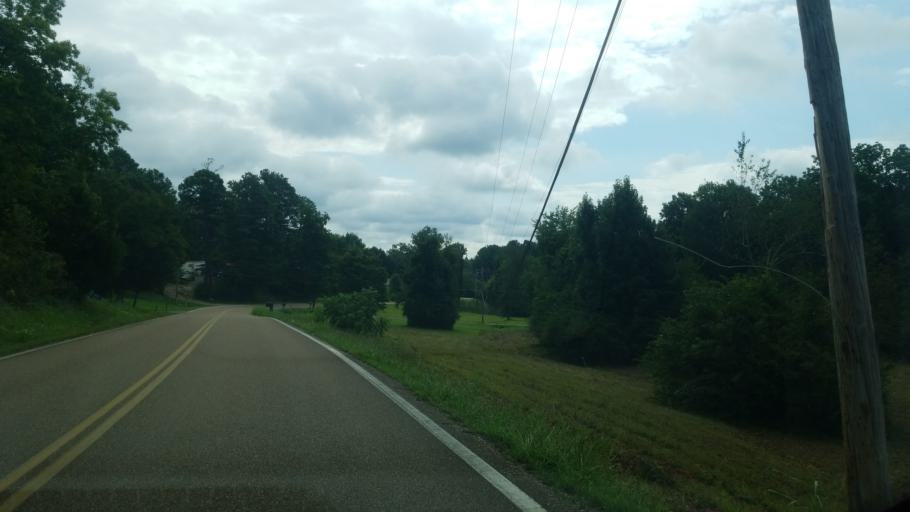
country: US
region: Tennessee
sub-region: Hamilton County
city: Lakesite
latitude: 35.2055
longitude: -85.0760
